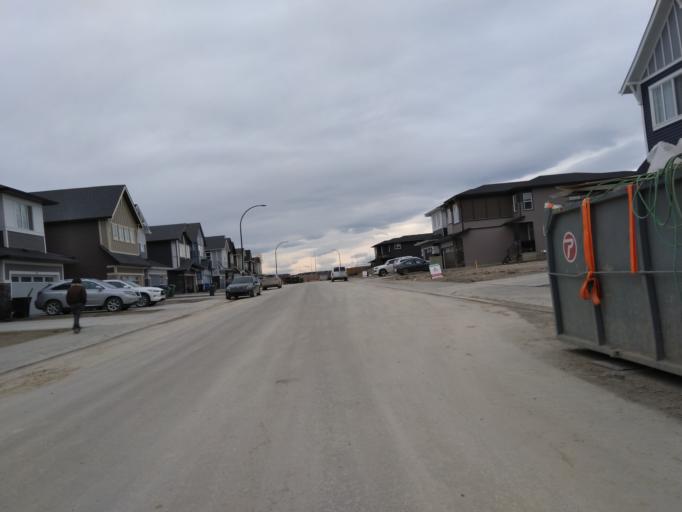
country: CA
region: Alberta
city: Calgary
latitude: 51.1783
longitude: -114.0871
